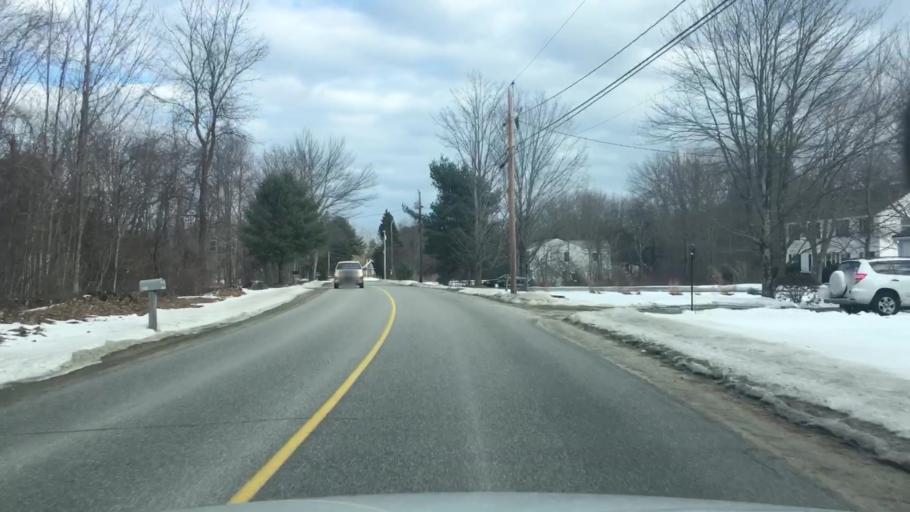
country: US
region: Maine
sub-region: York County
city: Kennebunk
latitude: 43.4056
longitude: -70.5158
